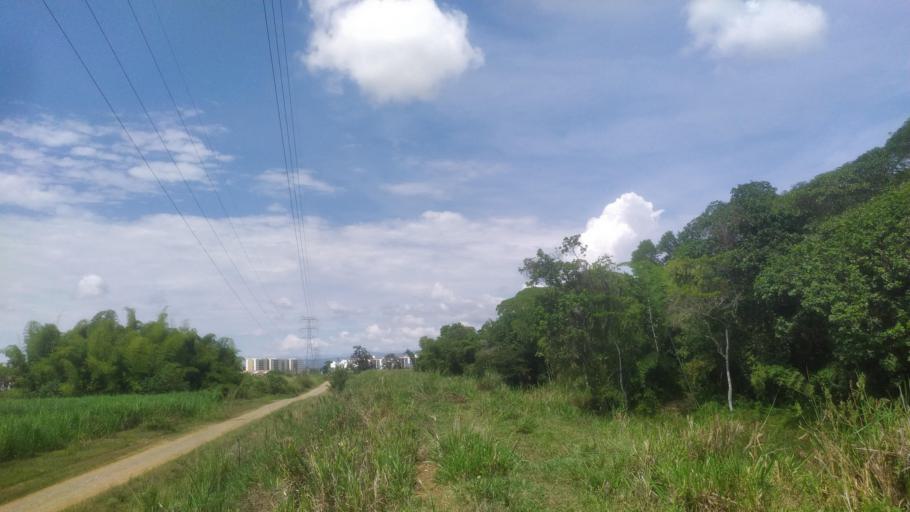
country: CO
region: Valle del Cauca
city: Jamundi
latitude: 3.2825
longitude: -76.5342
